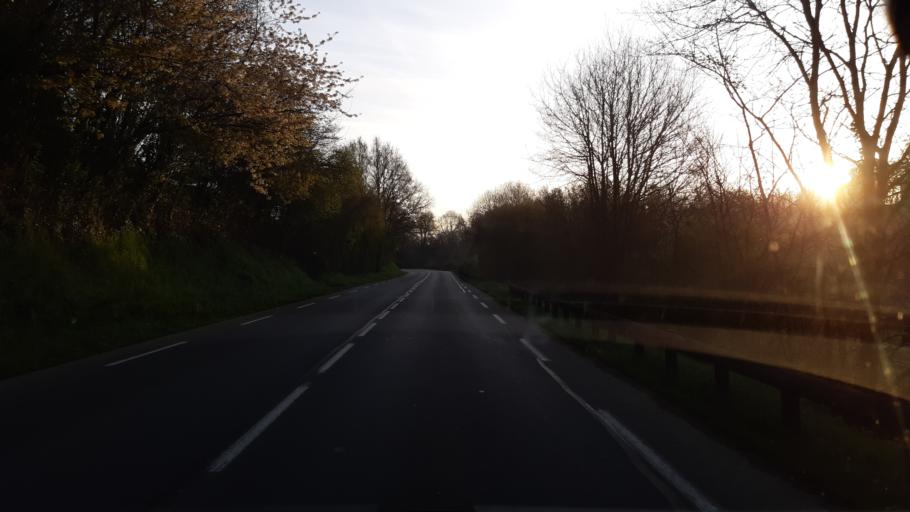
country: FR
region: Lower Normandy
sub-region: Departement de la Manche
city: Agneaux
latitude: 49.0781
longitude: -1.1234
